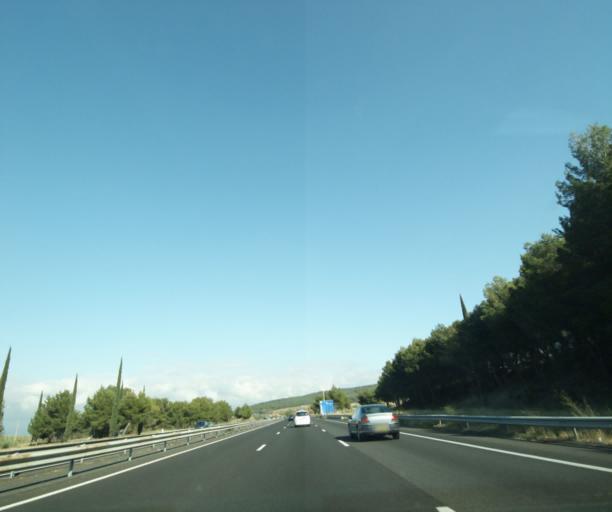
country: FR
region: Languedoc-Roussillon
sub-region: Departement de l'Aude
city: Vinassan
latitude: 43.1906
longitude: 3.0674
